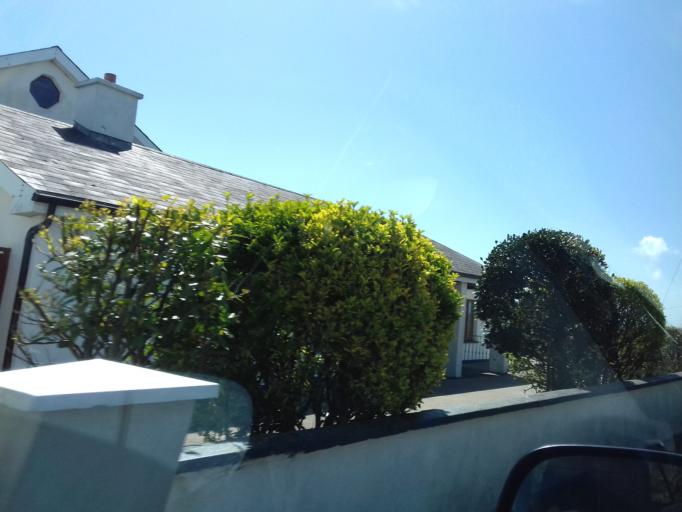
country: IE
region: Munster
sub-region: Waterford
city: Dunmore East
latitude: 52.1945
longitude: -6.8548
